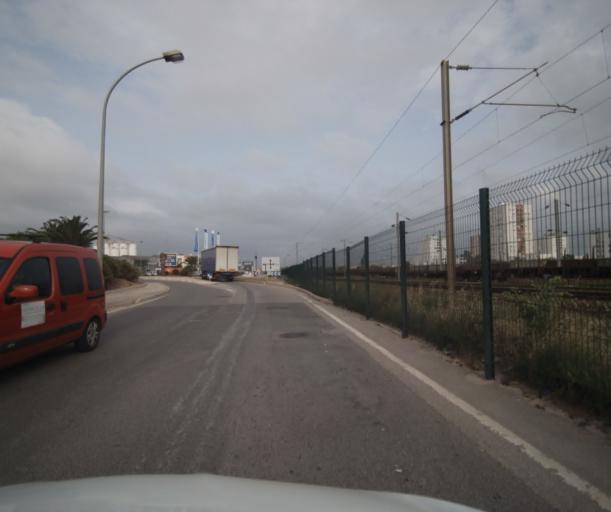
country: FR
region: Provence-Alpes-Cote d'Azur
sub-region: Departement du Var
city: Six-Fours-les-Plages
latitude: 43.1167
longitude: 5.8622
